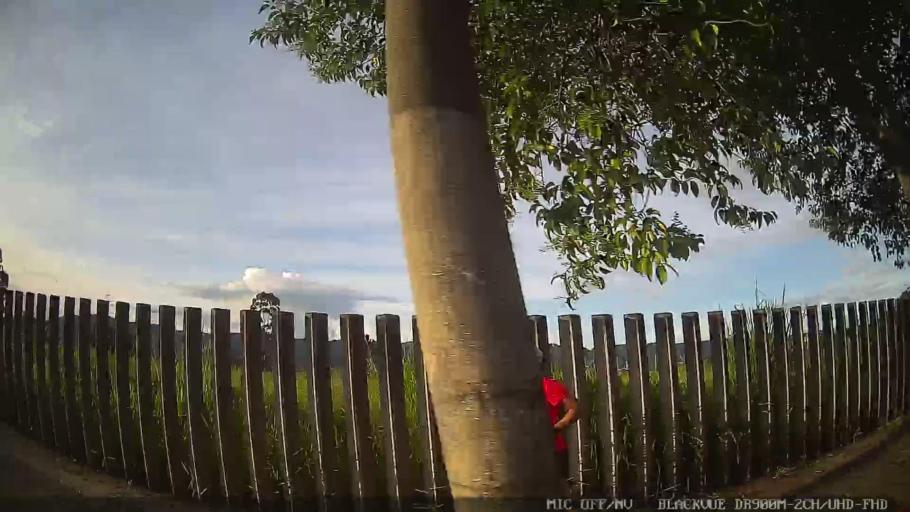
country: BR
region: Sao Paulo
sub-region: Mogi das Cruzes
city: Mogi das Cruzes
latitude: -23.5132
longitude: -46.1626
